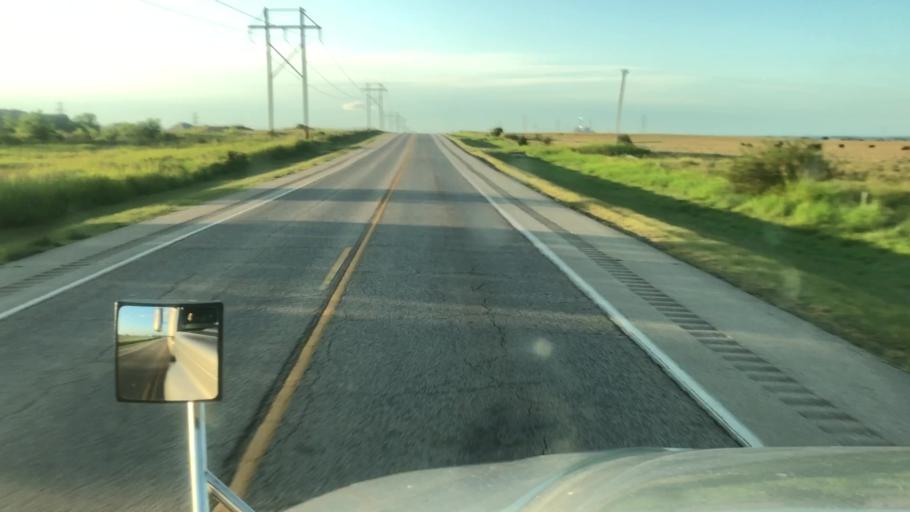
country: US
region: Oklahoma
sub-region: Noble County
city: Perry
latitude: 36.3903
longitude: -97.0677
